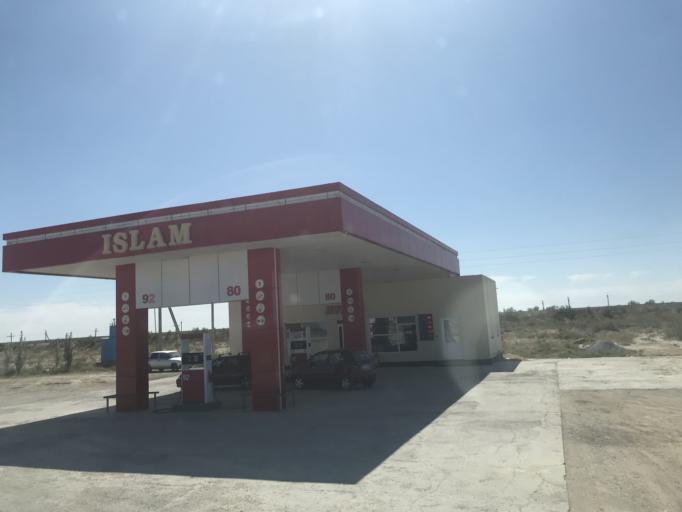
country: KZ
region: Qyzylorda
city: Belkol
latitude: 44.7648
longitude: 65.7783
